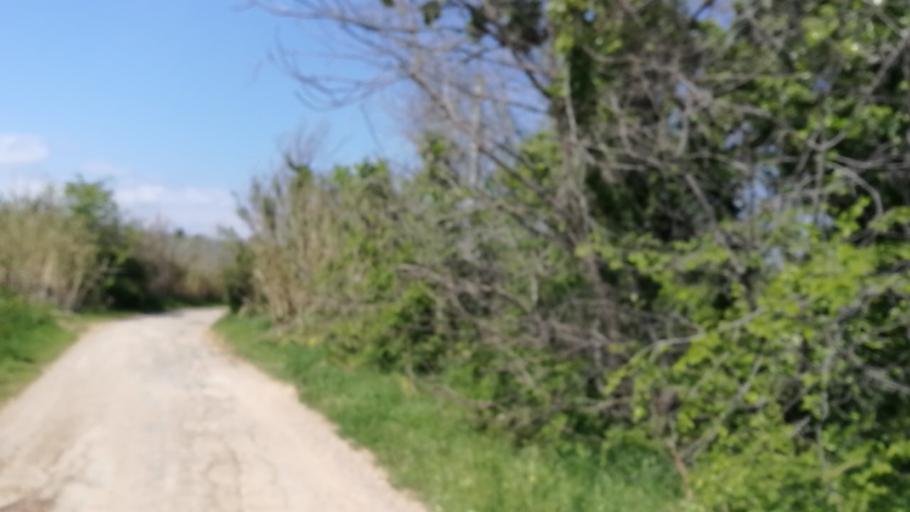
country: IT
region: Molise
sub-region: Provincia di Campobasso
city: Termoli
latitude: 41.9714
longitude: 14.9871
